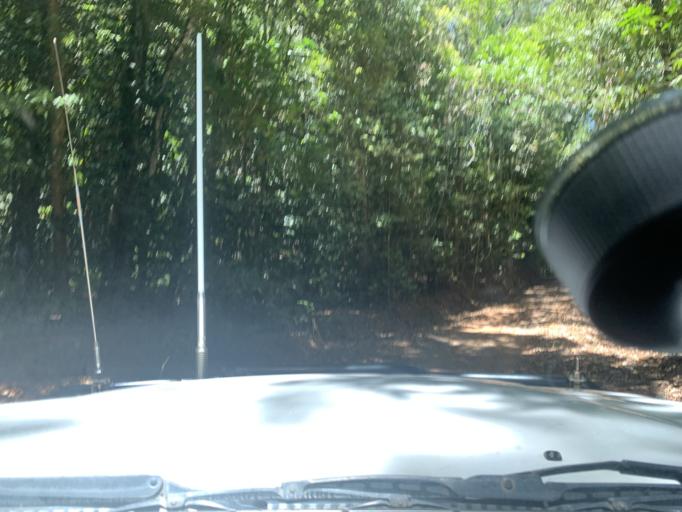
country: AU
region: Queensland
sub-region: Cairns
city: Redlynch
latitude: -16.9712
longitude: 145.6499
